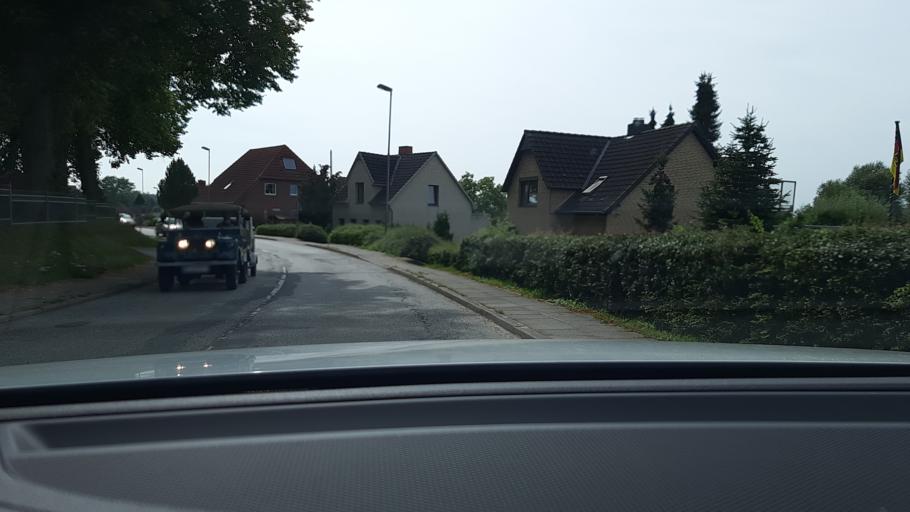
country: DE
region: Schleswig-Holstein
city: Reinfeld
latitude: 53.8256
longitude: 10.4768
